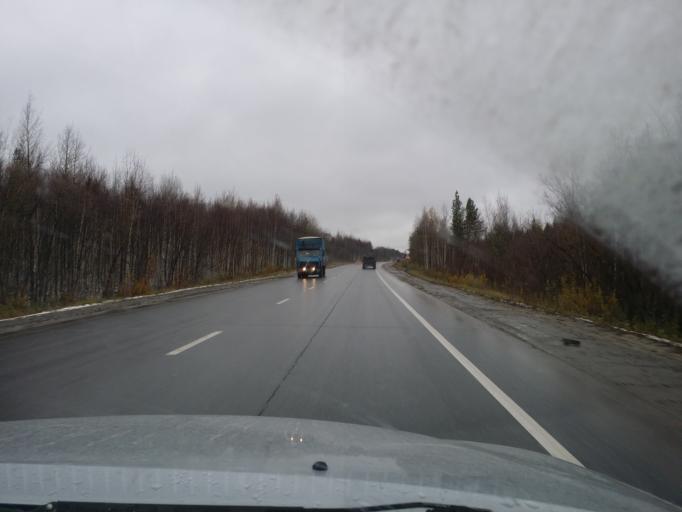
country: RU
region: Khanty-Mansiyskiy Avtonomnyy Okrug
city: Megion
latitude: 61.0928
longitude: 76.0831
